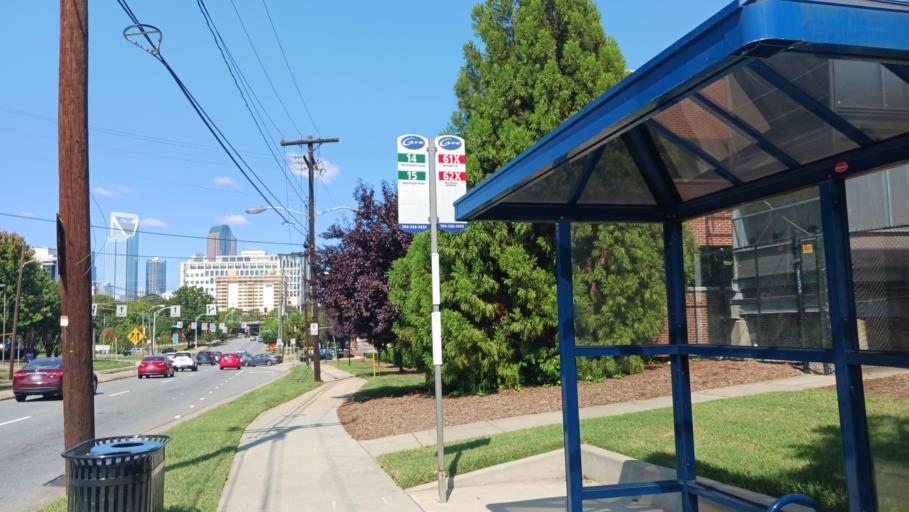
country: US
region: North Carolina
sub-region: Mecklenburg County
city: Charlotte
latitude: 35.2158
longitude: -80.8314
